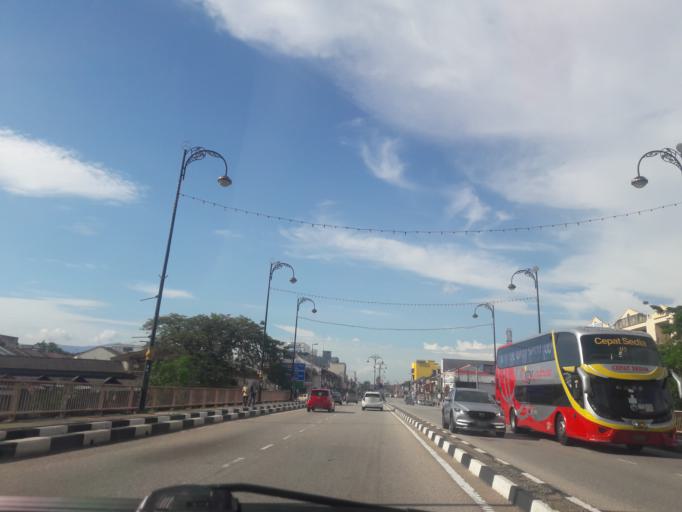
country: MY
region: Kedah
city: Sungai Petani
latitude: 5.6387
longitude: 100.4886
